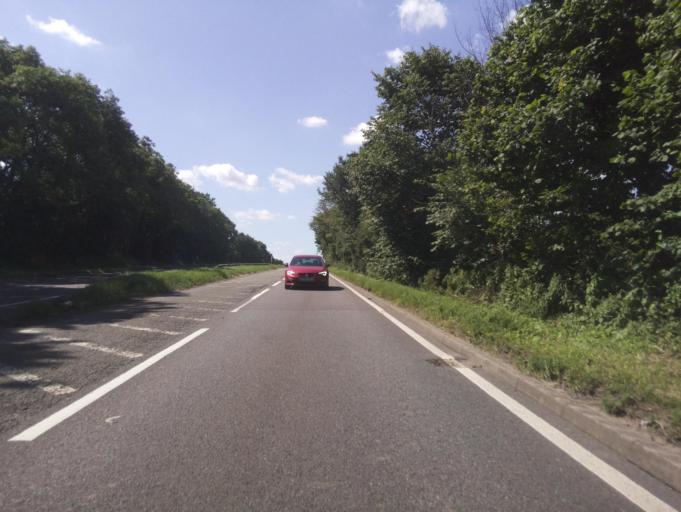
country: GB
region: England
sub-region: Warwickshire
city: Atherstone
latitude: 52.5839
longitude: -1.5687
